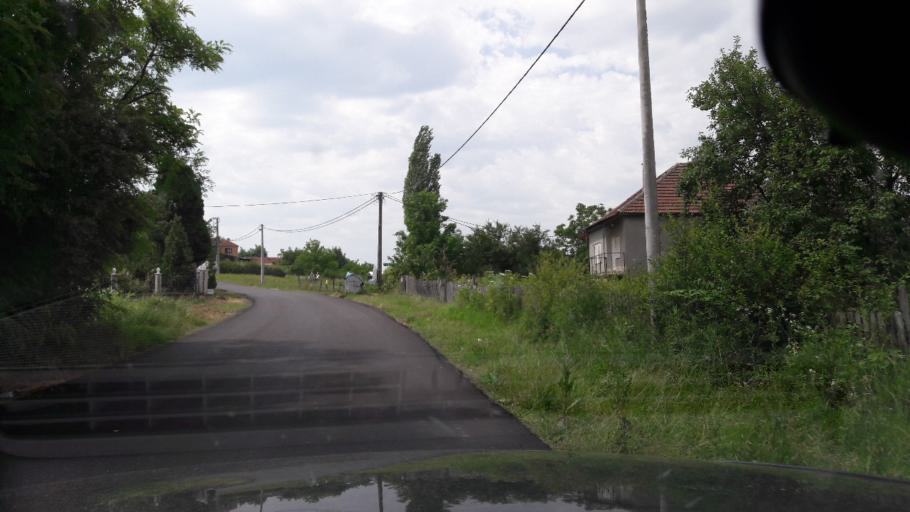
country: RS
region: Central Serbia
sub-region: Belgrade
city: Sopot
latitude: 44.6047
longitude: 20.6012
